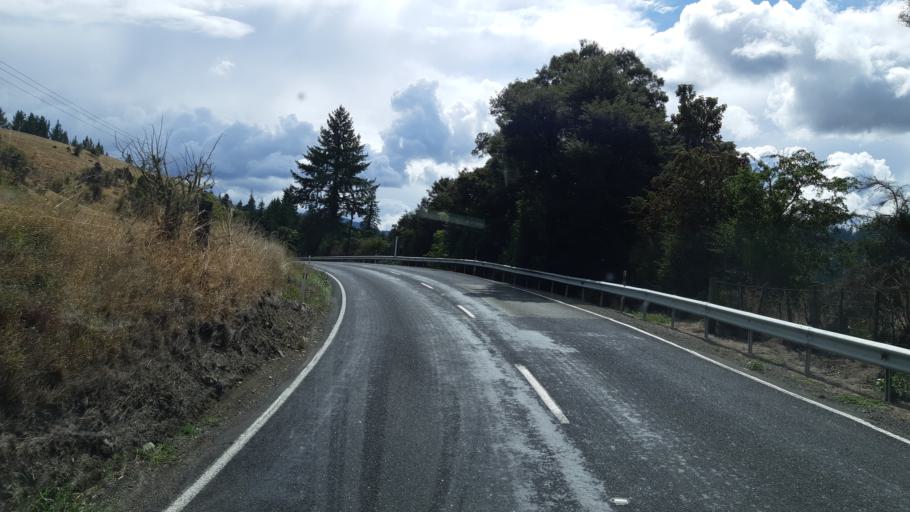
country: NZ
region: Tasman
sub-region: Tasman District
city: Wakefield
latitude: -41.5057
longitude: 172.7949
